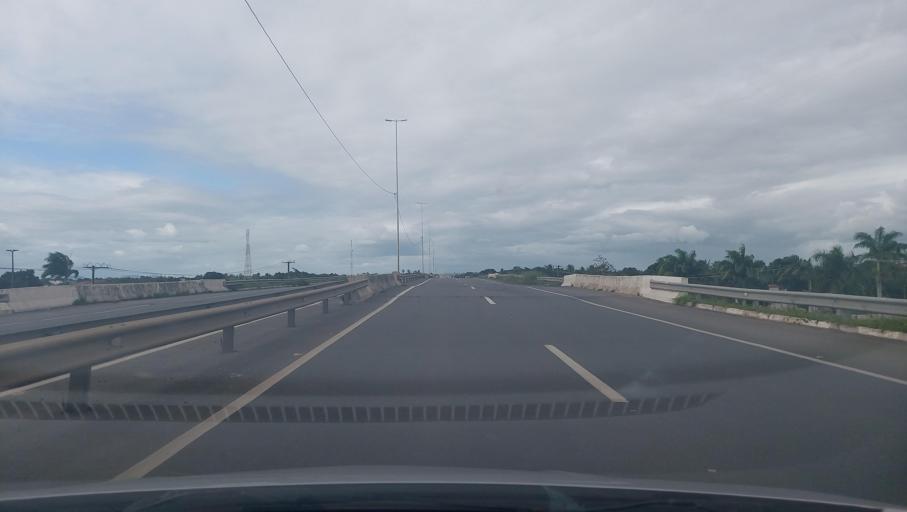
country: BR
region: Bahia
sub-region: Santo Estevao
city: Santo Estevao
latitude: -12.4470
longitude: -39.2432
